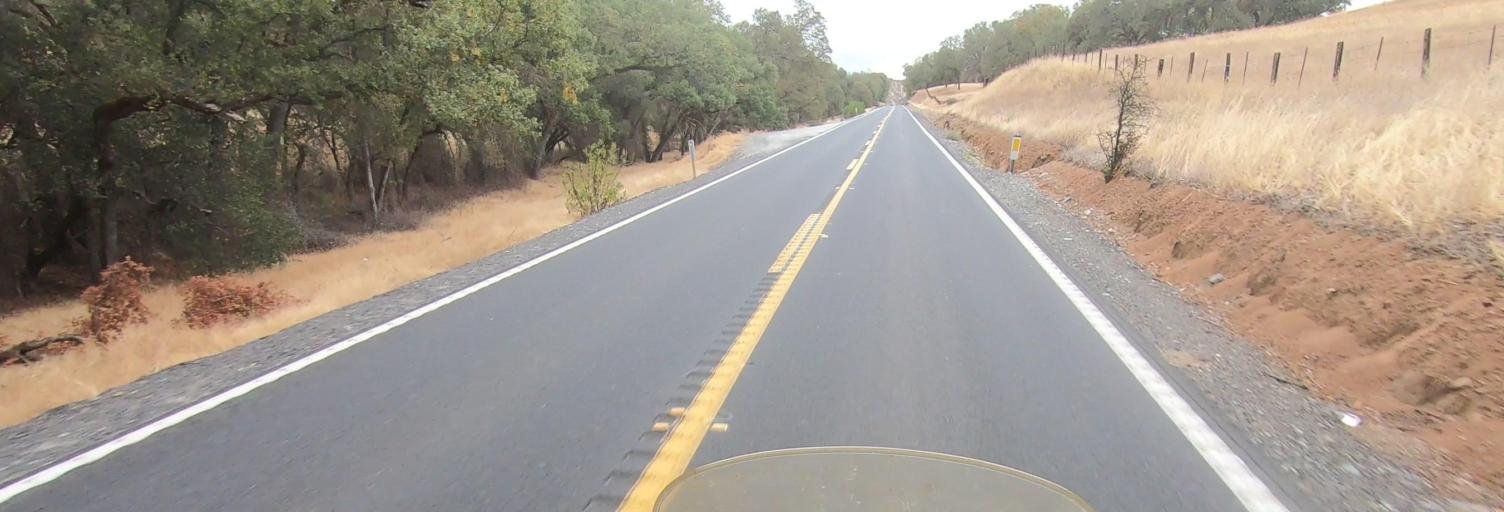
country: US
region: California
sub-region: Calaveras County
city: Angels Camp
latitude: 38.1137
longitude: -120.6117
